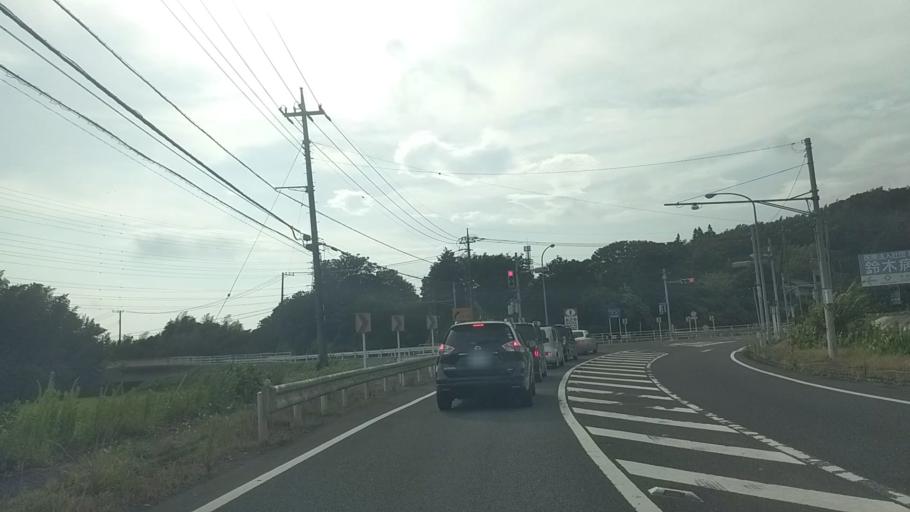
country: JP
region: Chiba
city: Kimitsu
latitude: 35.3108
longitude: 139.9631
